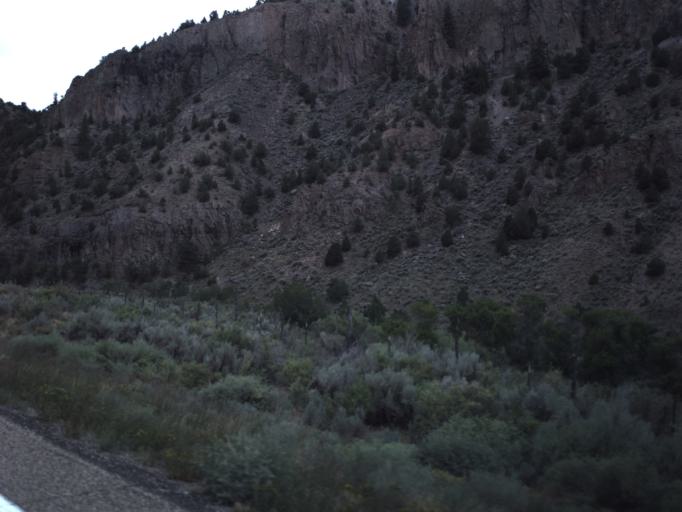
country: US
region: Utah
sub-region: Piute County
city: Junction
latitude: 38.1899
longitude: -112.1017
